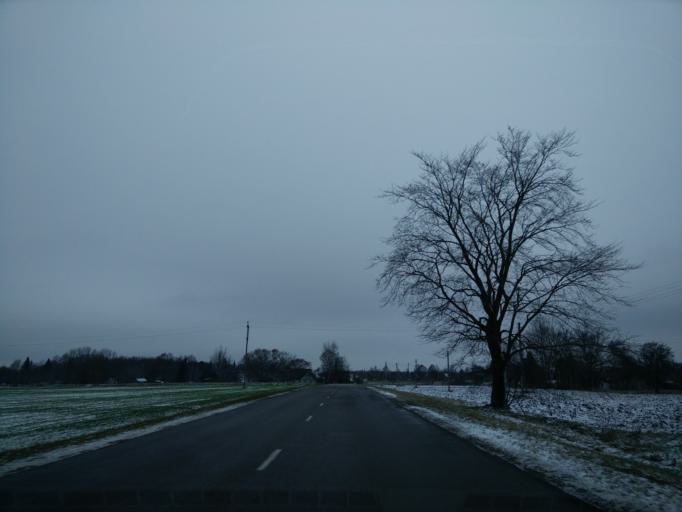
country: LT
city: Ariogala
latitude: 55.3858
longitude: 23.3454
